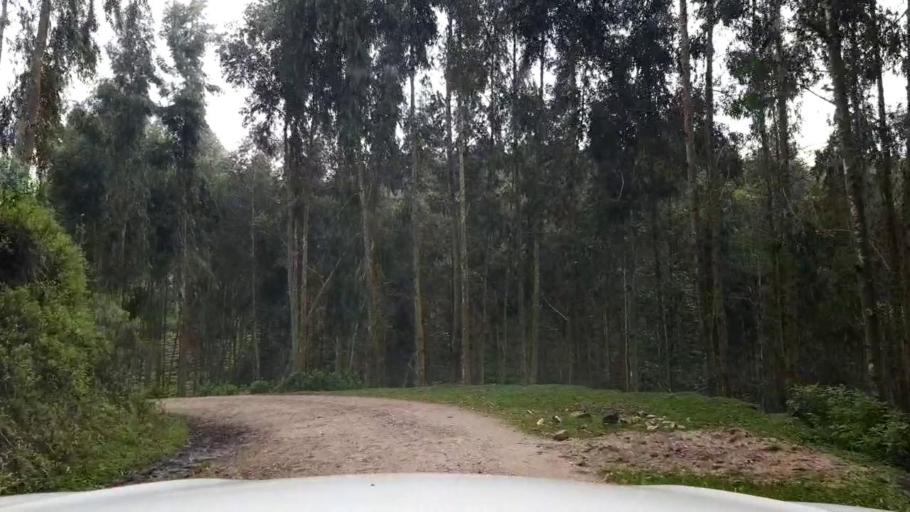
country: RW
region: Western Province
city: Gisenyi
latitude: -1.6854
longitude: 29.4175
